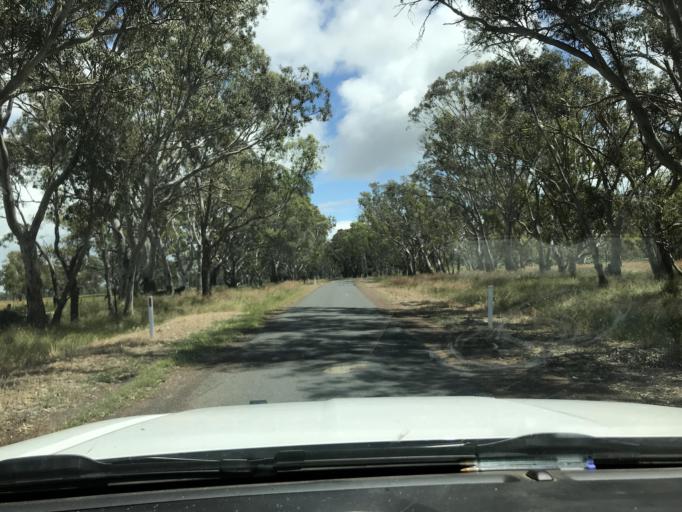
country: AU
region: Victoria
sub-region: Horsham
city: Horsham
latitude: -37.1065
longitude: 141.7490
